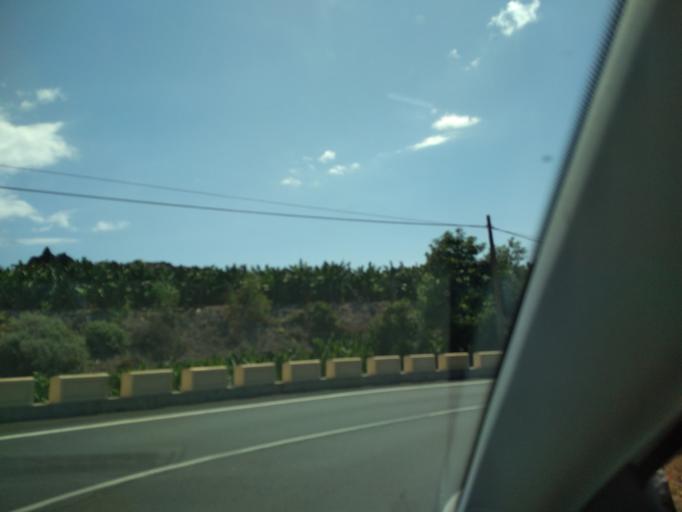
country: ES
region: Canary Islands
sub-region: Provincia de Santa Cruz de Tenerife
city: Santiago del Teide
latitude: 28.2389
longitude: -16.8367
